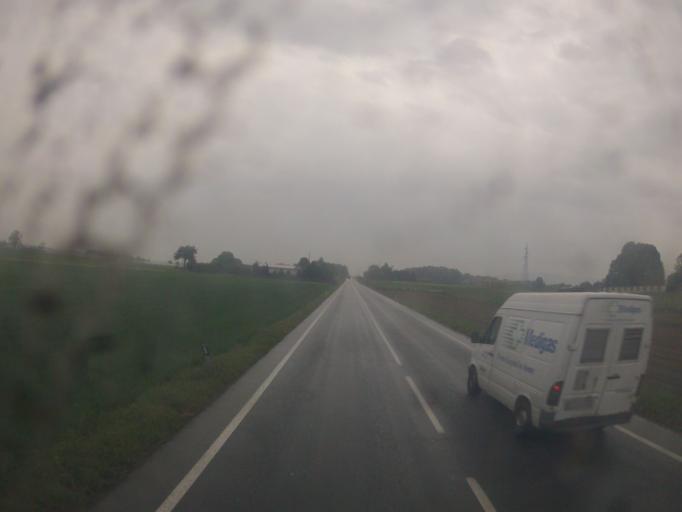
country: IT
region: Piedmont
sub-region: Provincia di Torino
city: La Loggia
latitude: 44.9317
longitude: 7.6720
